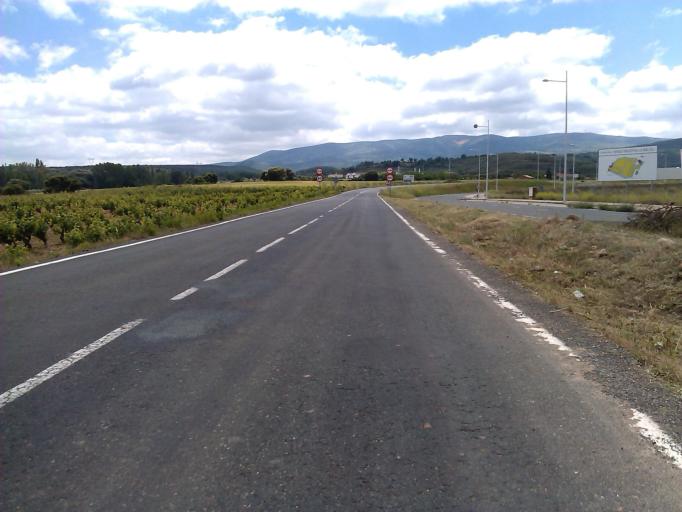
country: ES
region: La Rioja
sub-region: Provincia de La Rioja
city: Hornos de Moncalvillo
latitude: 42.4136
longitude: -2.5924
